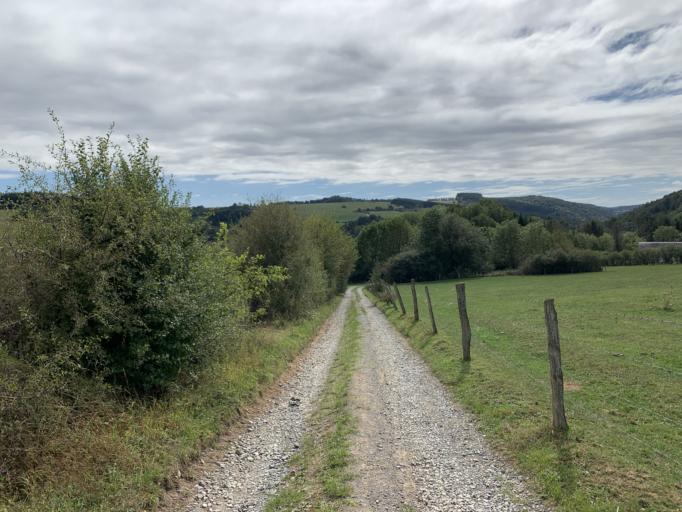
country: BE
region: Wallonia
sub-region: Province du Luxembourg
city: Tellin
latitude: 50.0965
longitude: 5.2792
